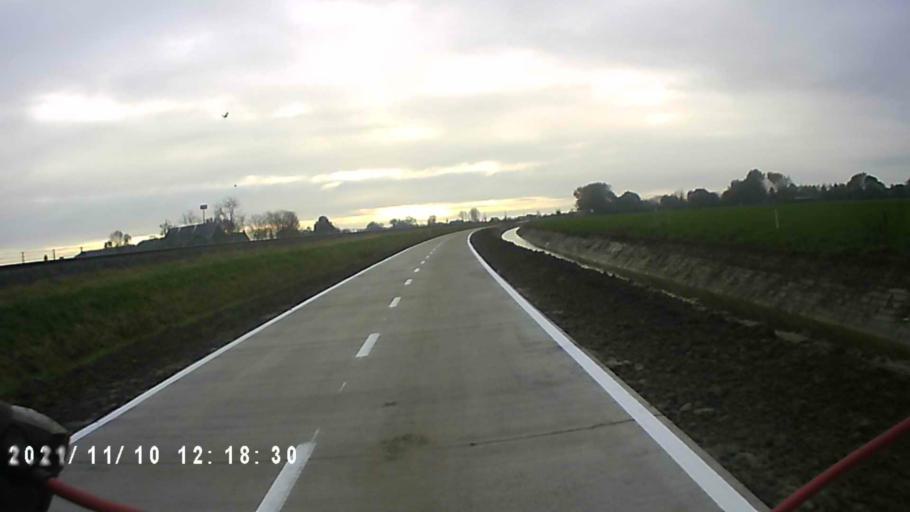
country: NL
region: Groningen
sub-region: Gemeente Winsum
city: Winsum
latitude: 53.2999
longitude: 6.5399
